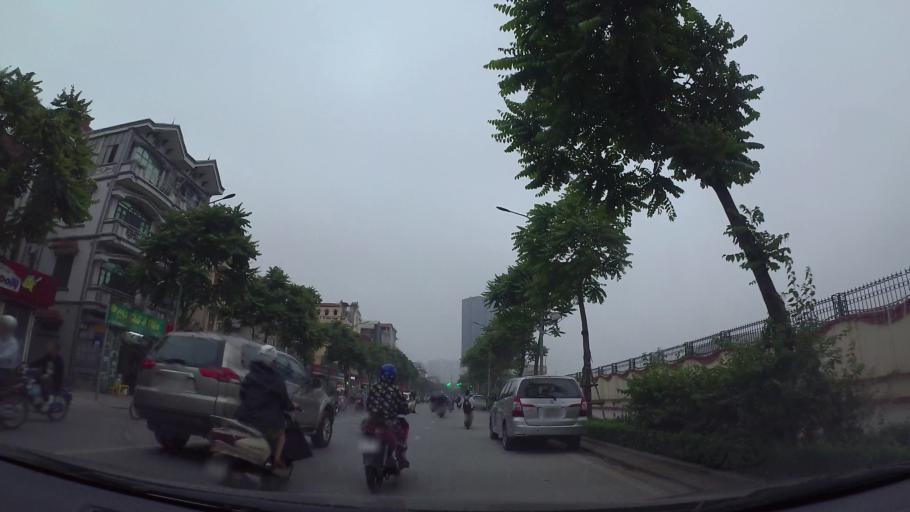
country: VN
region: Ha Noi
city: Dong Da
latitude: 20.9961
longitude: 105.8301
